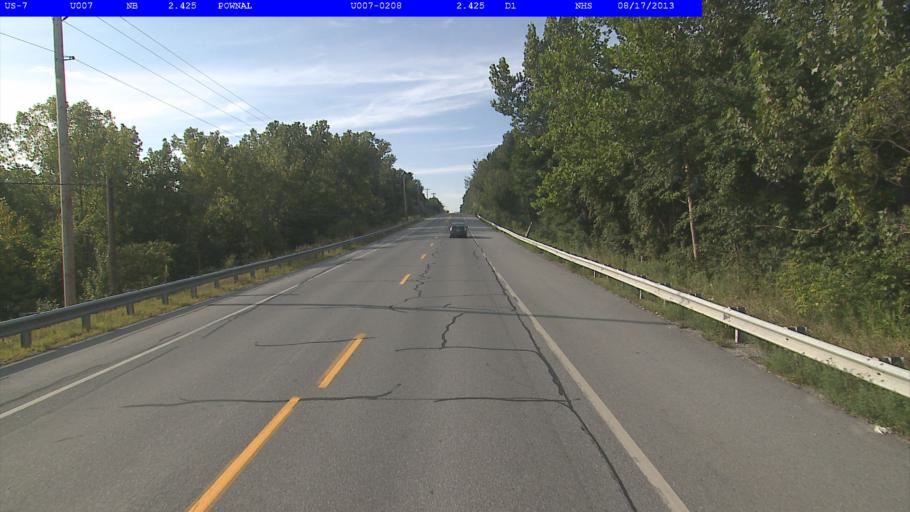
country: US
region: Massachusetts
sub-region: Berkshire County
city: Williamstown
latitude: 42.7709
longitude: -73.2365
